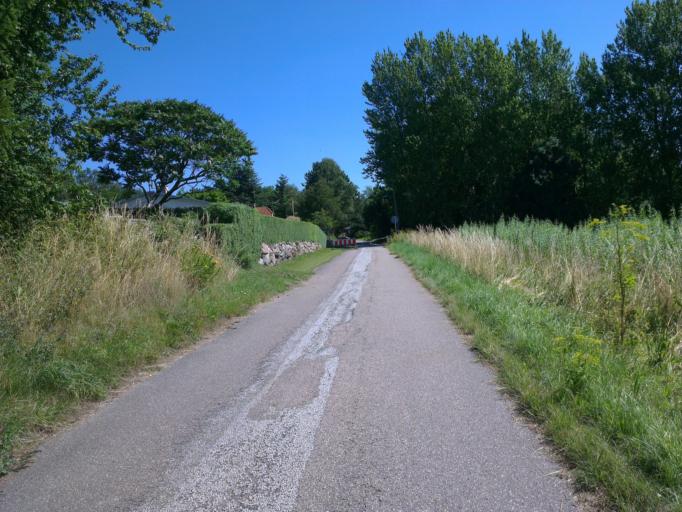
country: DK
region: Capital Region
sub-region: Frederikssund Kommune
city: Slangerup
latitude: 55.8295
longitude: 12.1819
